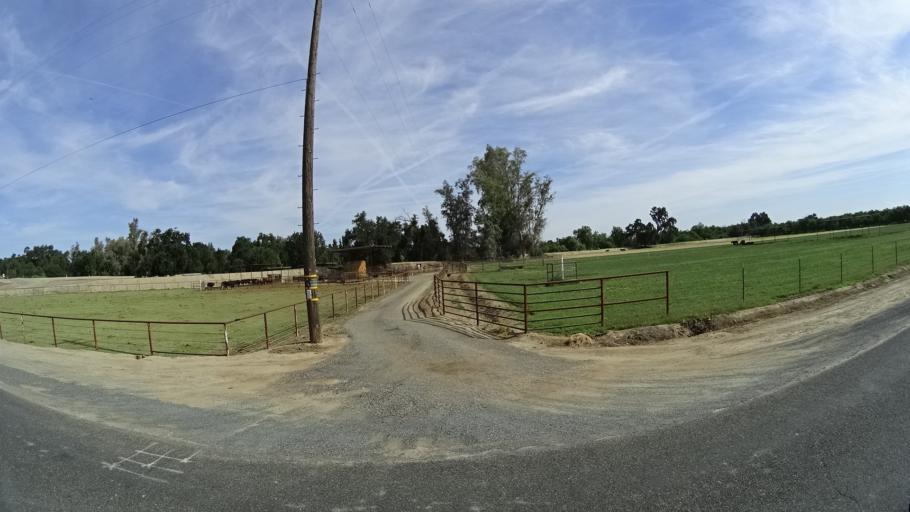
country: US
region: California
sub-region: Fresno County
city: Laton
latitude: 36.4157
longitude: -119.6665
